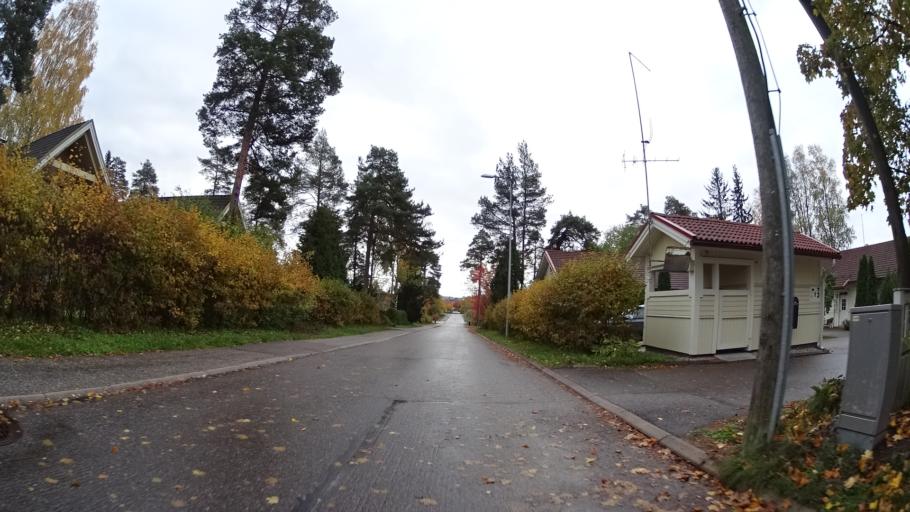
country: FI
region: Uusimaa
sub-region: Helsinki
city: Espoo
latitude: 60.2167
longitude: 24.6455
